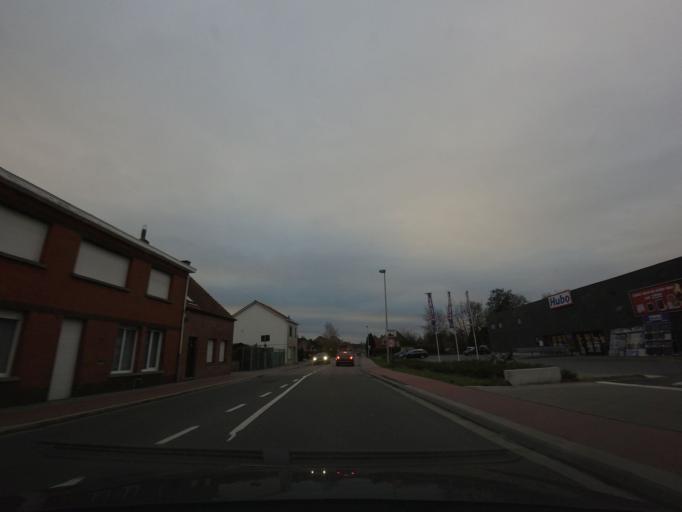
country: BE
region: Flanders
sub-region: Provincie Antwerpen
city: Brecht
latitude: 51.3567
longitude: 4.6413
